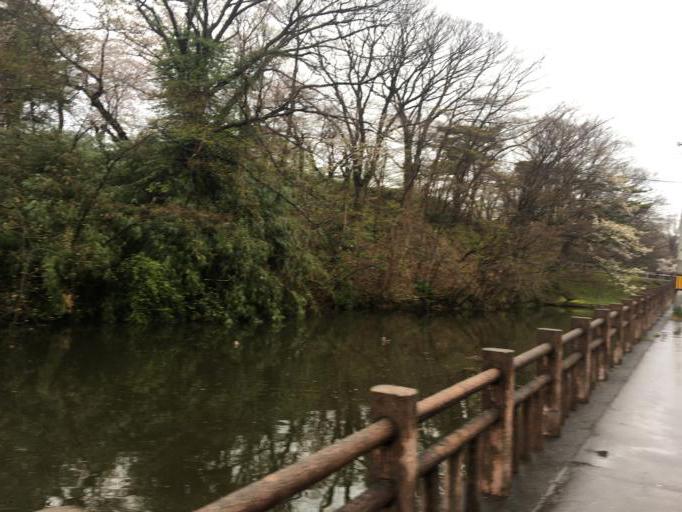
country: JP
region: Akita
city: Akita
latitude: 39.7195
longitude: 140.1255
